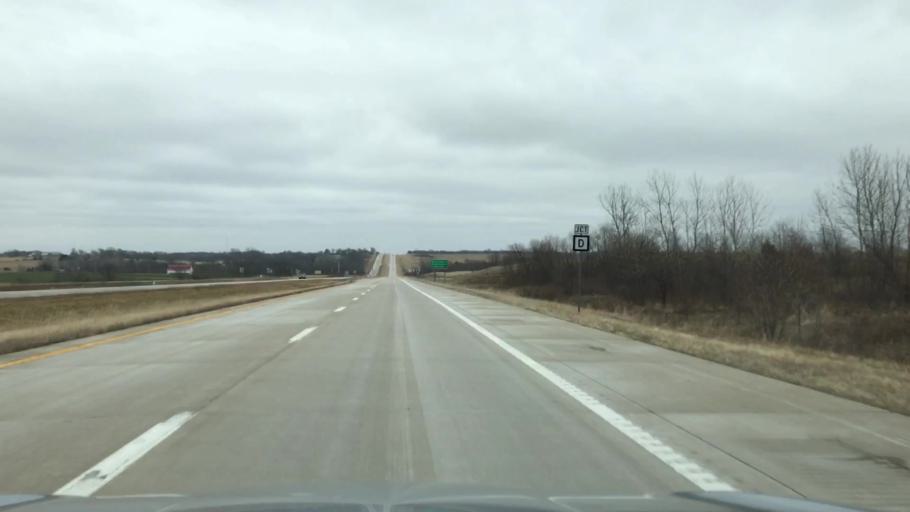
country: US
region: Missouri
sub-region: Livingston County
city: Chillicothe
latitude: 39.7373
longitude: -93.7120
